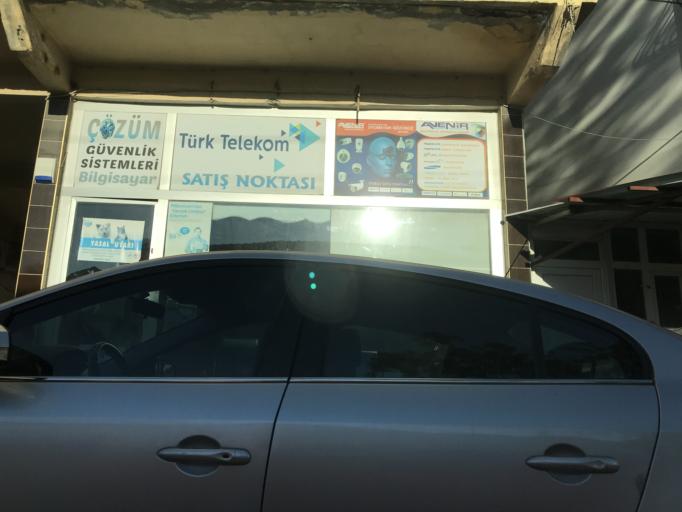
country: TR
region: Hatay
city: Samandag
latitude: 36.0822
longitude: 35.9810
